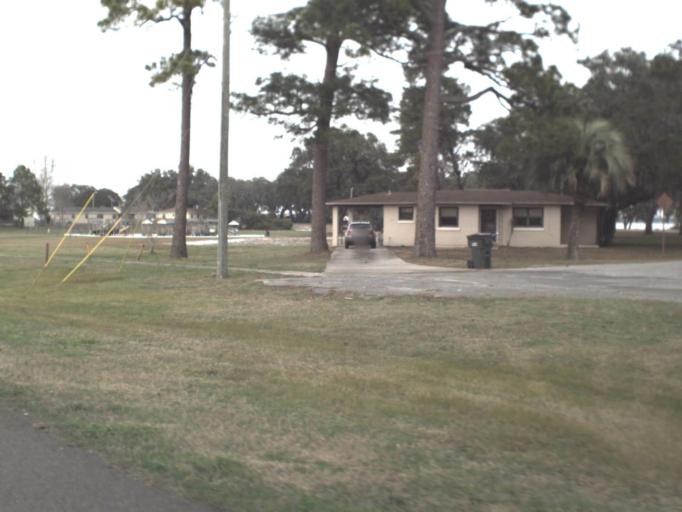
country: US
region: Florida
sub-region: Bay County
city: Tyndall Air Force Base
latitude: 30.0918
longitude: -85.6110
